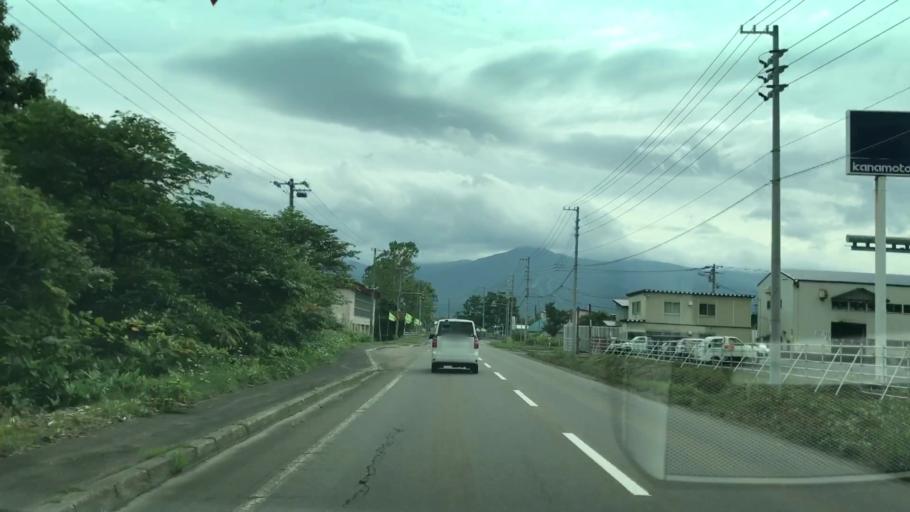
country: JP
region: Hokkaido
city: Iwanai
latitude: 43.0091
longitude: 140.5430
